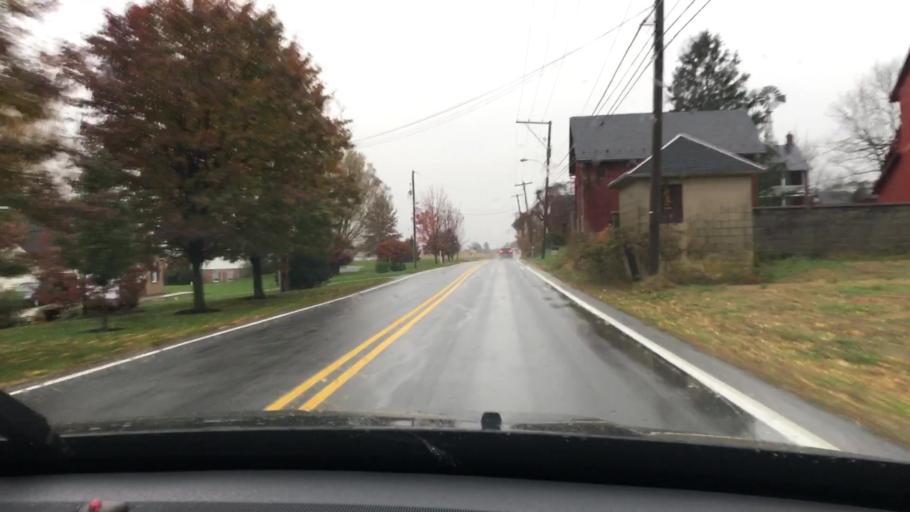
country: US
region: Pennsylvania
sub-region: York County
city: Stewartstown
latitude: 39.7320
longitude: -76.5109
